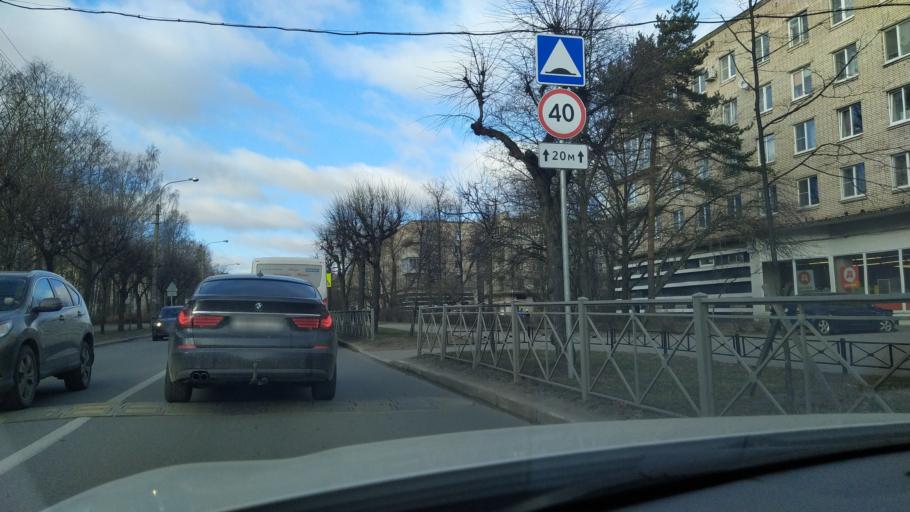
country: RU
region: St.-Petersburg
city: Pushkin
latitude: 59.7279
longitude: 30.4139
